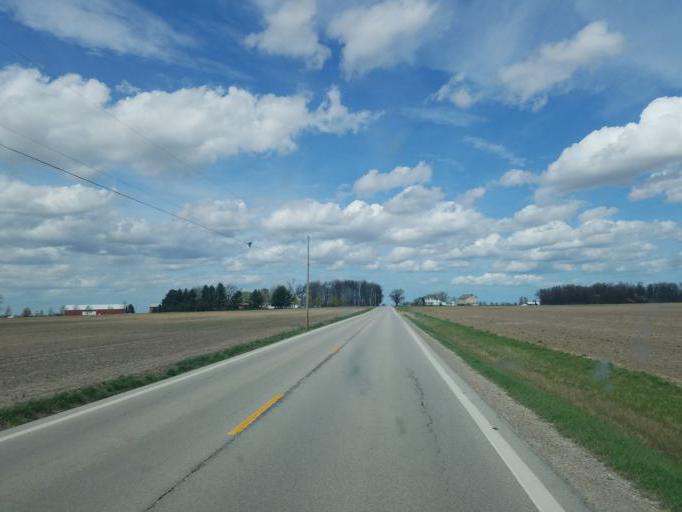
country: US
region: Ohio
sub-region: Huron County
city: Bellevue
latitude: 41.2435
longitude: -82.8046
